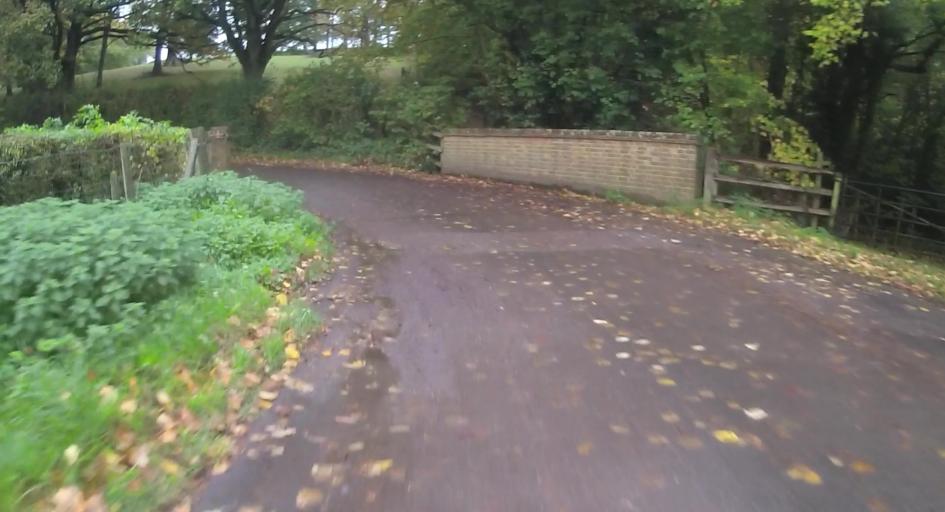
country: GB
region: England
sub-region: Surrey
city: Farnham
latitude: 51.2199
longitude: -0.8321
